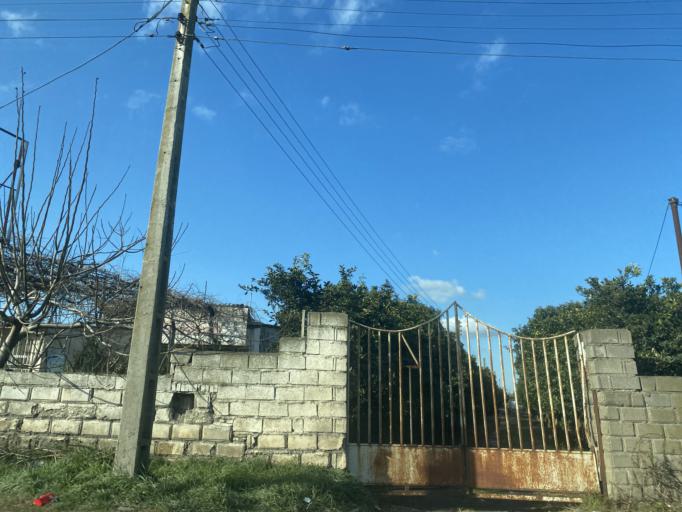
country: IR
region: Mazandaran
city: Babol
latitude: 36.5268
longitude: 52.6203
